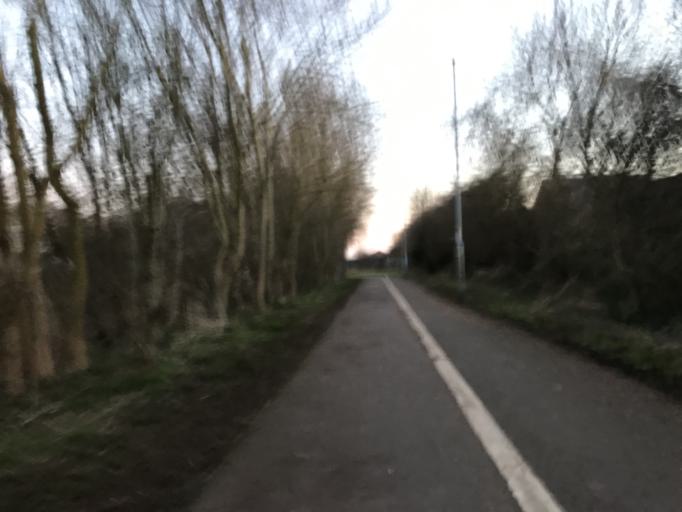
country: GB
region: England
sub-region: Lincolnshire
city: Holton le Clay
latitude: 53.5260
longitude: -0.0646
